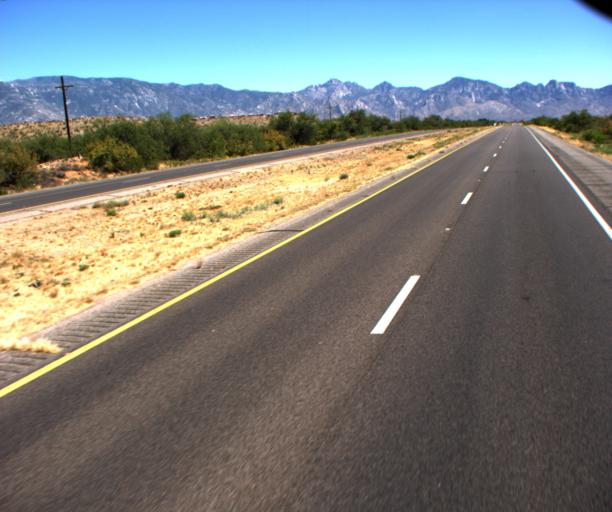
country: US
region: Arizona
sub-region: Pima County
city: Catalina
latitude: 32.5352
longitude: -110.9307
